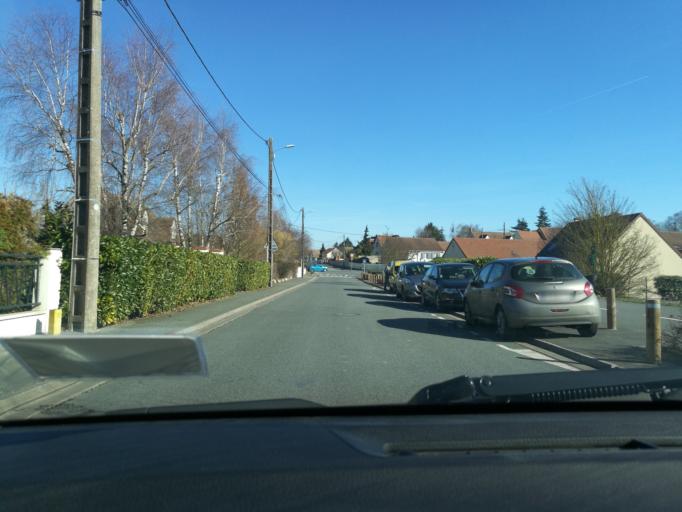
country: FR
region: Centre
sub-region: Departement du Loiret
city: Saint-Ay
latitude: 47.8628
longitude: 1.7570
